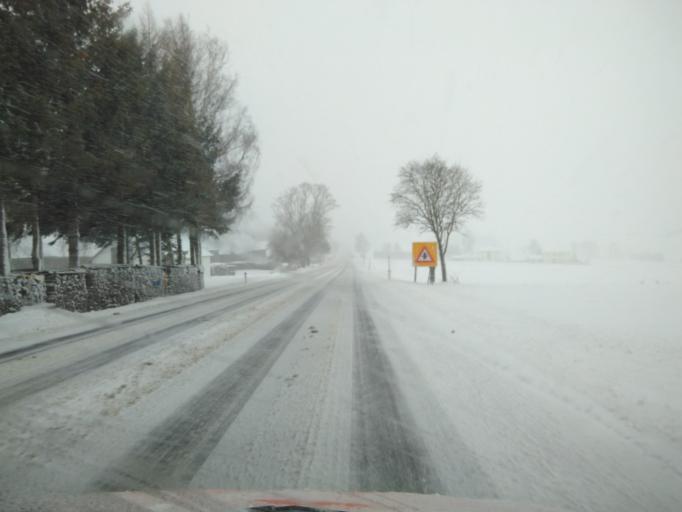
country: AT
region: Upper Austria
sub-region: Politischer Bezirk Urfahr-Umgebung
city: Bad Leonfelden
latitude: 48.5096
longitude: 14.2949
